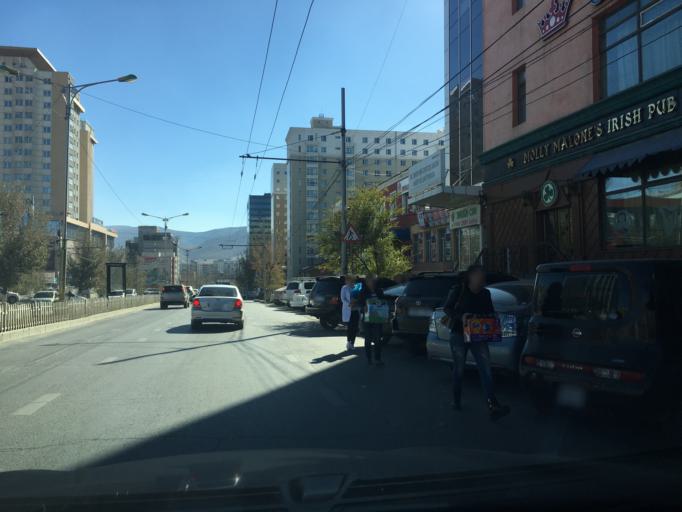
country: MN
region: Ulaanbaatar
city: Ulaanbaatar
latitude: 47.9174
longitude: 106.8909
